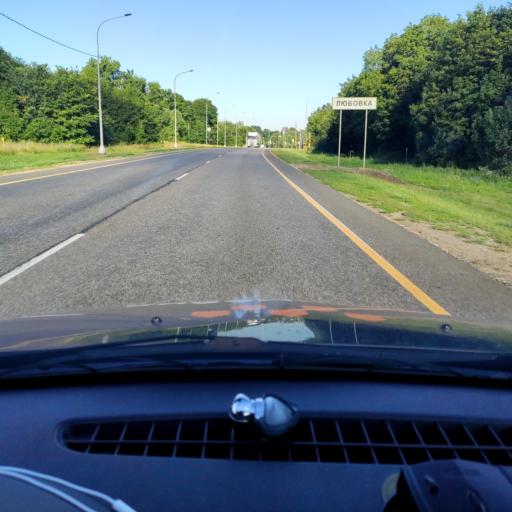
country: RU
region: Orjol
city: Pokrovskoye
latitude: 52.6195
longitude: 36.7448
